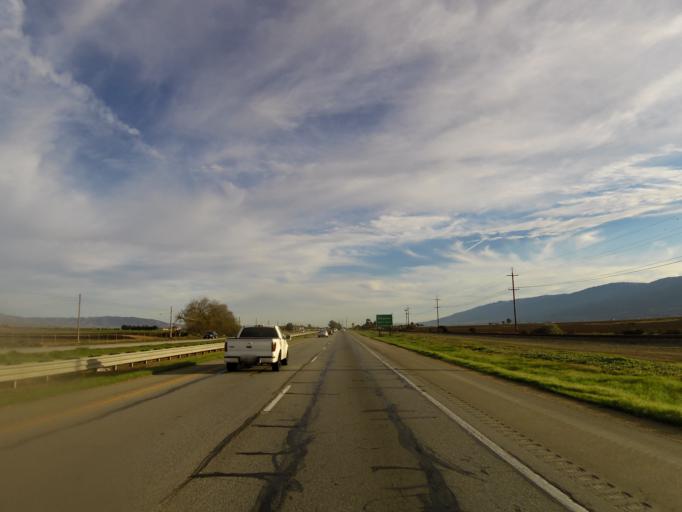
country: US
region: California
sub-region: Monterey County
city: Chualar
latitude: 36.5778
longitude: -121.5274
